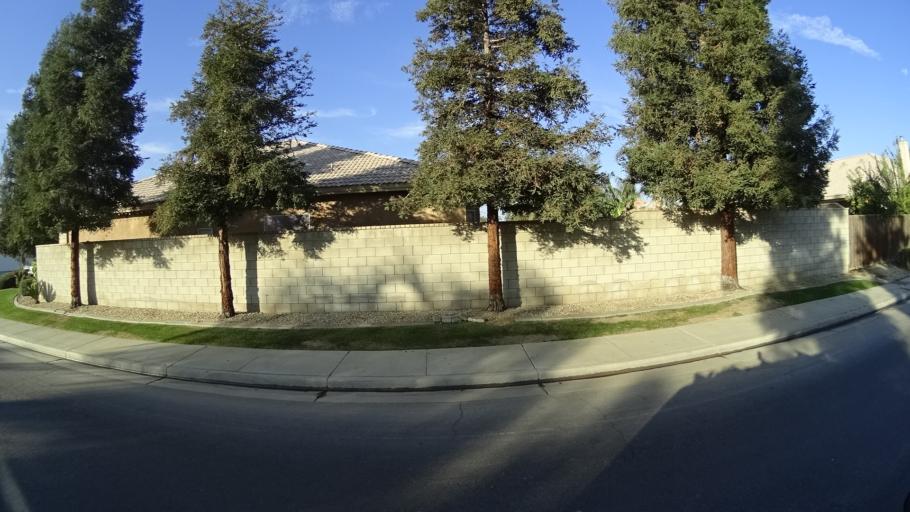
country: US
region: California
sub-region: Kern County
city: Greenfield
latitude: 35.2730
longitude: -119.0523
